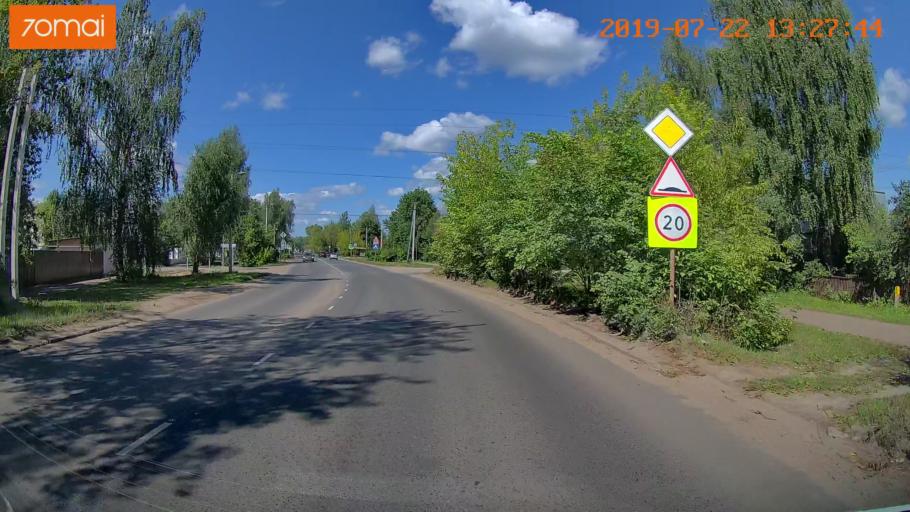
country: RU
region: Ivanovo
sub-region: Gorod Ivanovo
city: Ivanovo
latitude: 57.0377
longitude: 40.9507
